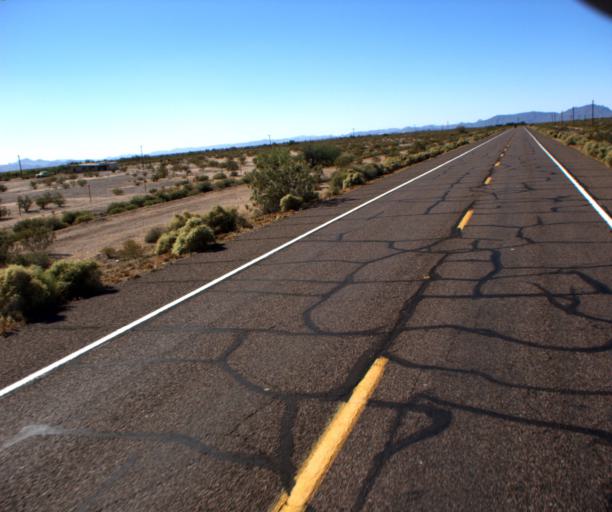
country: US
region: Arizona
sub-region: Maricopa County
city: Gila Bend
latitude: 32.9219
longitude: -112.7347
